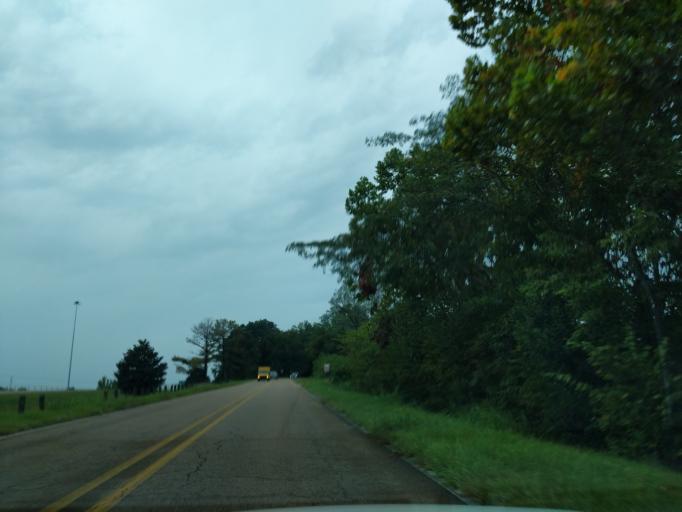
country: US
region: Mississippi
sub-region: Warren County
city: Vicksburg
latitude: 32.3173
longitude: -90.8822
